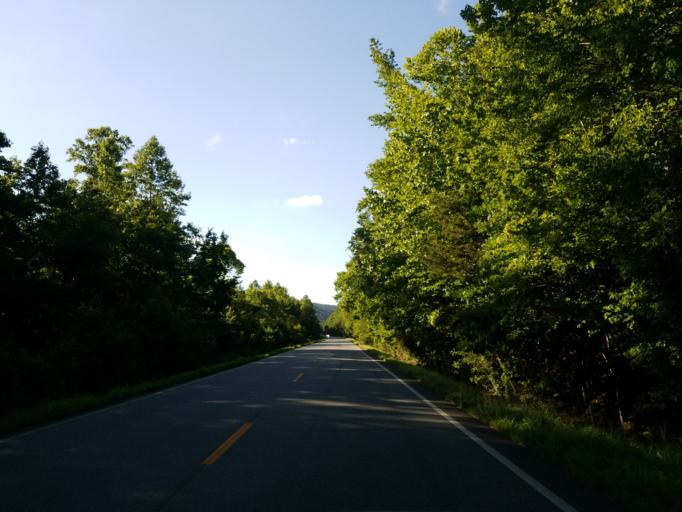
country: US
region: Georgia
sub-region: Gordon County
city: Calhoun
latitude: 34.6290
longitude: -85.0573
